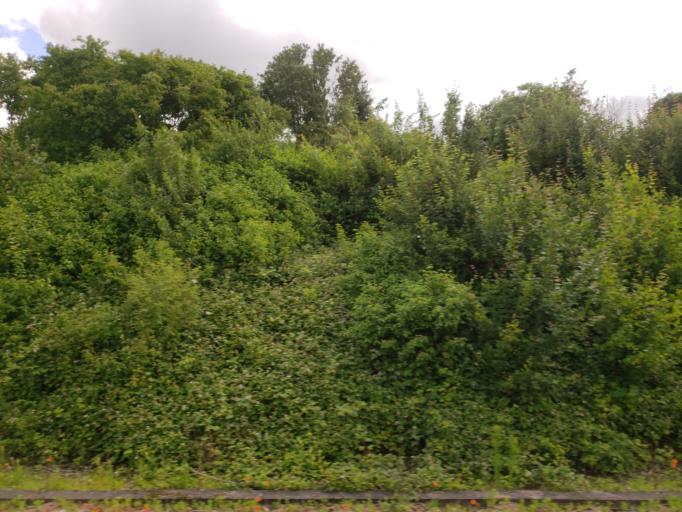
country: FR
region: Ile-de-France
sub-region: Departement du Val-d'Oise
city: Roissy-en-France
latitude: 48.9870
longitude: 2.5210
